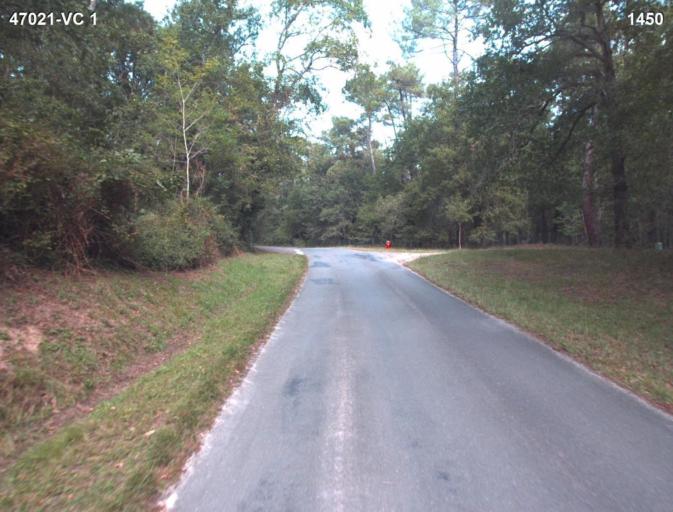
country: FR
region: Aquitaine
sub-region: Departement du Lot-et-Garonne
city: Barbaste
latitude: 44.1539
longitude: 0.2902
